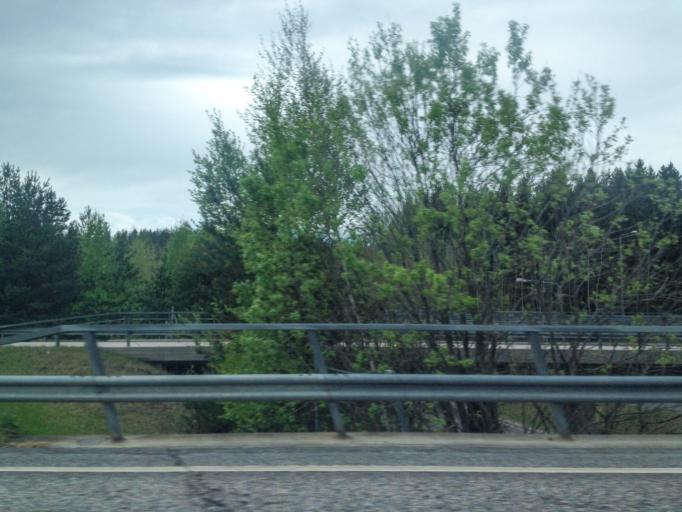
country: FI
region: Uusimaa
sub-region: Helsinki
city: Nurmijaervi
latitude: 60.4879
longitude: 24.8509
